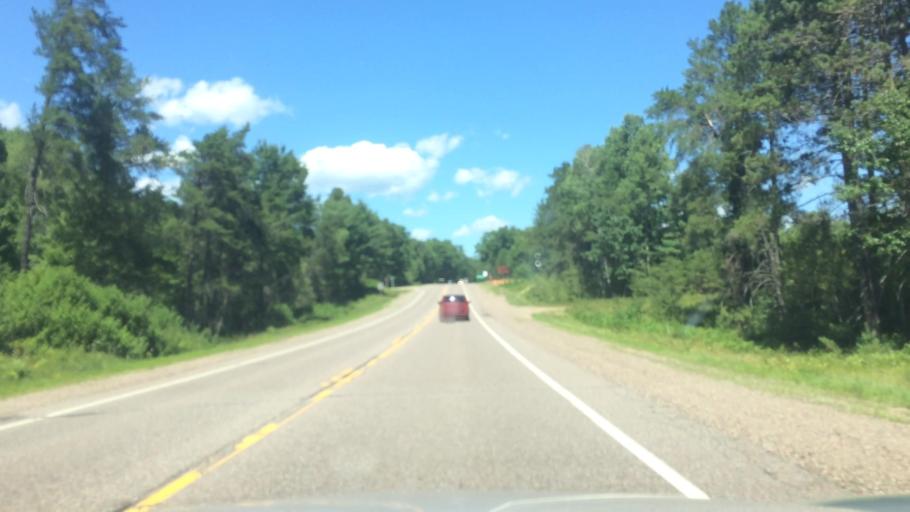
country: US
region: Wisconsin
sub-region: Vilas County
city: Lac du Flambeau
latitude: 45.7768
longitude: -89.7152
